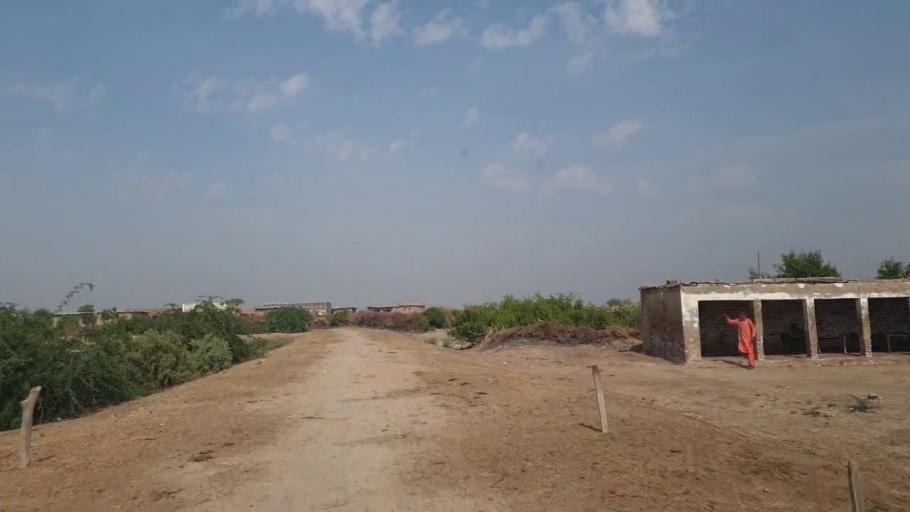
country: PK
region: Sindh
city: Rajo Khanani
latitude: 24.9892
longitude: 68.9757
